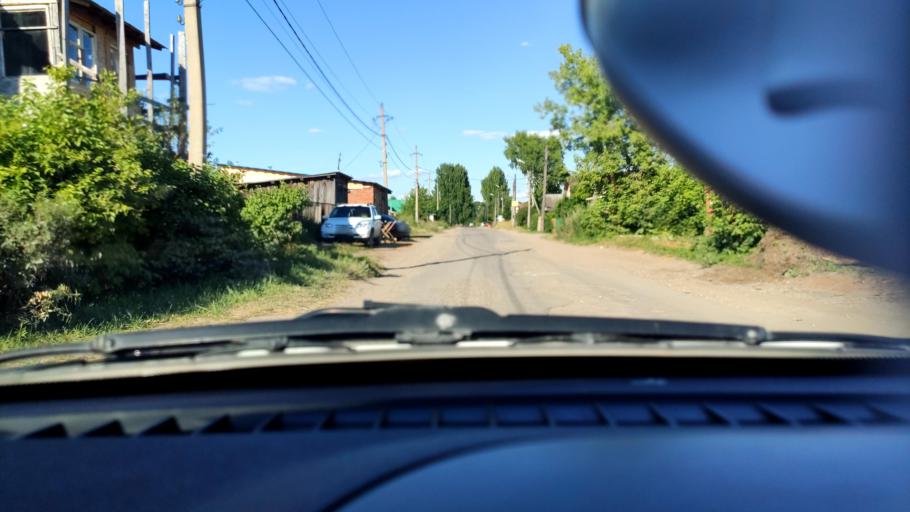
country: RU
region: Perm
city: Krasnokamsk
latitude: 58.0763
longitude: 55.8072
